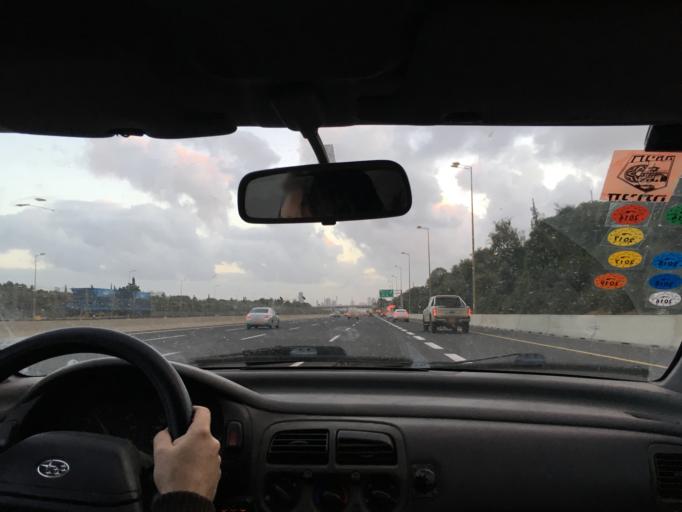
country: IL
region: Tel Aviv
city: Ramat HaSharon
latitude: 32.1255
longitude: 34.8098
